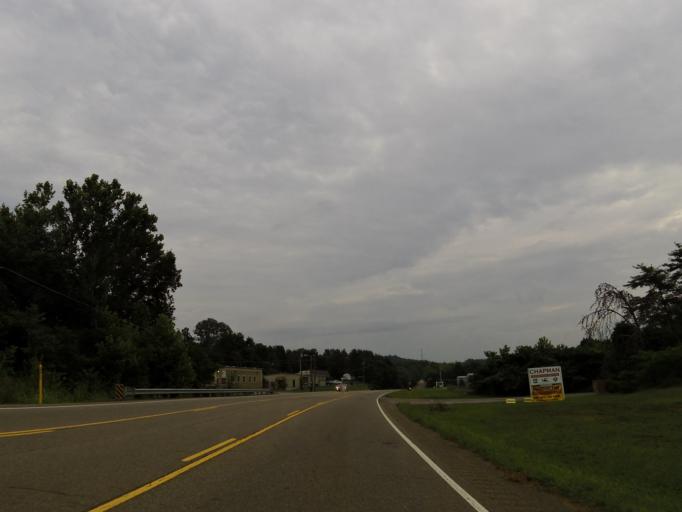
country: US
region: Tennessee
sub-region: Knox County
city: Knoxville
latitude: 35.9170
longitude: -83.8294
